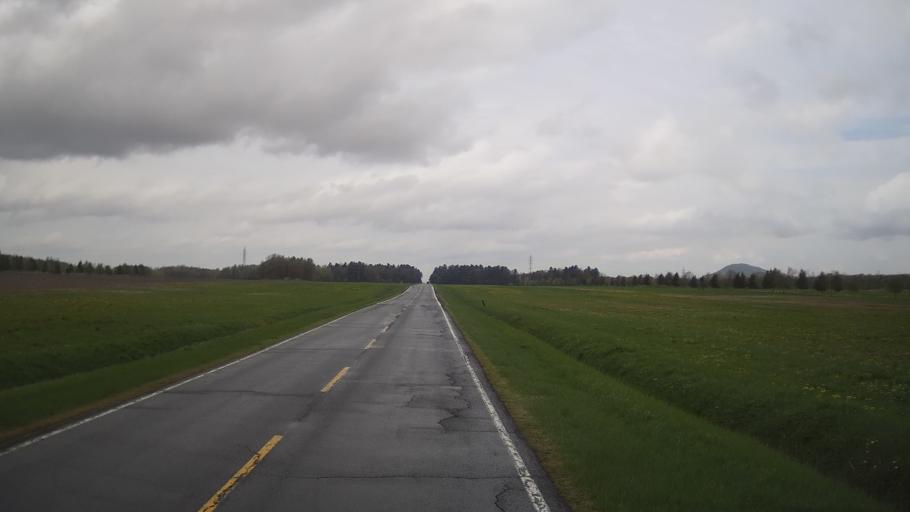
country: CA
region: Quebec
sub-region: Monteregie
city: Marieville
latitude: 45.3075
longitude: -73.1175
